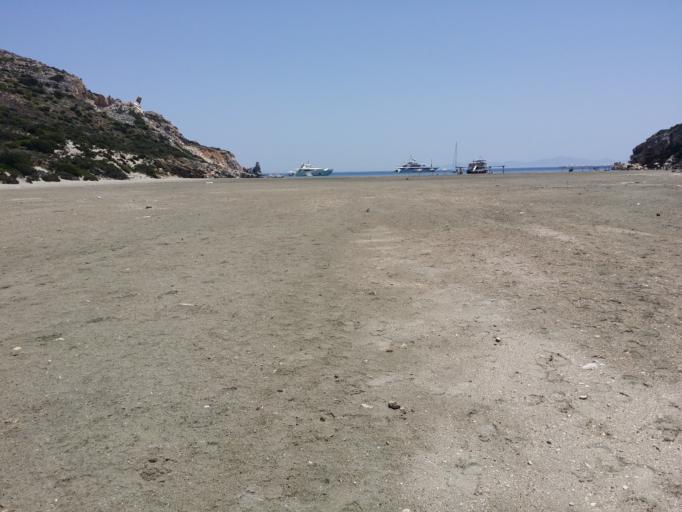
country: GR
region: South Aegean
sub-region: Nomos Kykladon
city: Antiparos
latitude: 36.9571
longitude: 24.9989
